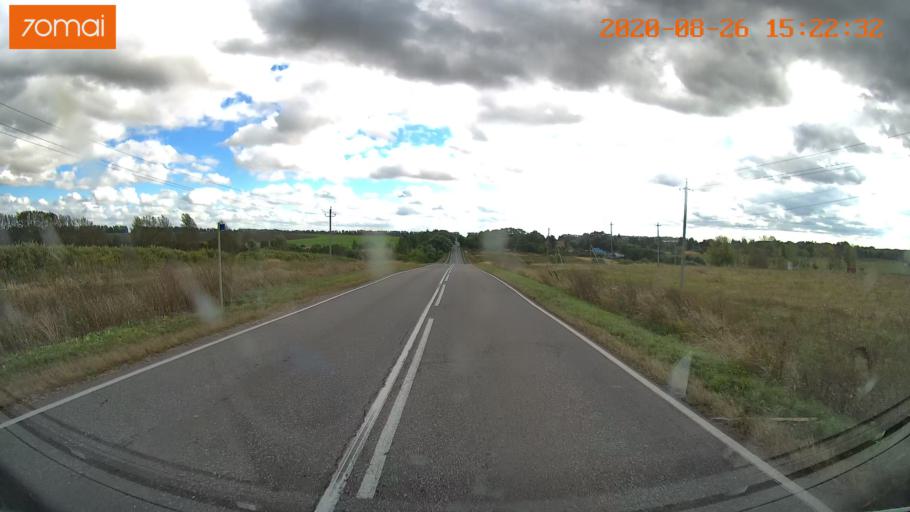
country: RU
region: Tula
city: Severo-Zadonsk
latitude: 54.1298
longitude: 38.4547
